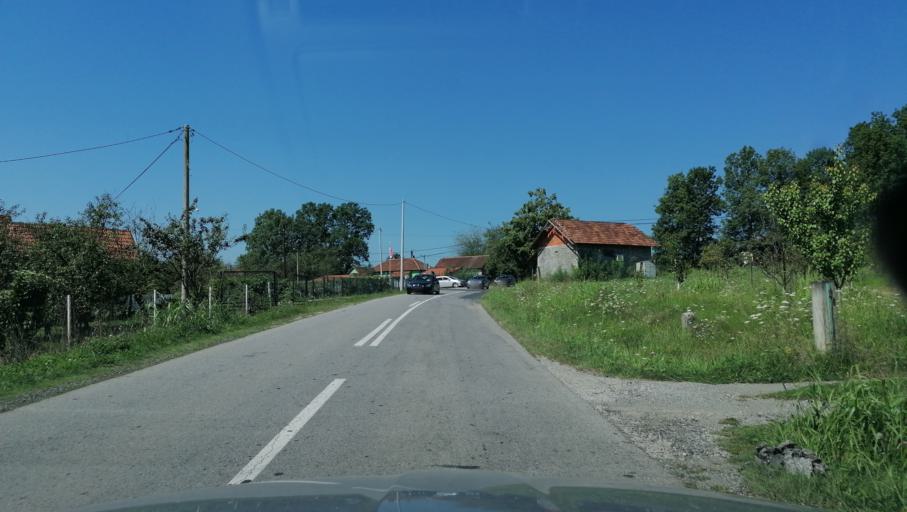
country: RS
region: Central Serbia
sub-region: Raski Okrug
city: Kraljevo
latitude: 43.7173
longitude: 20.8073
